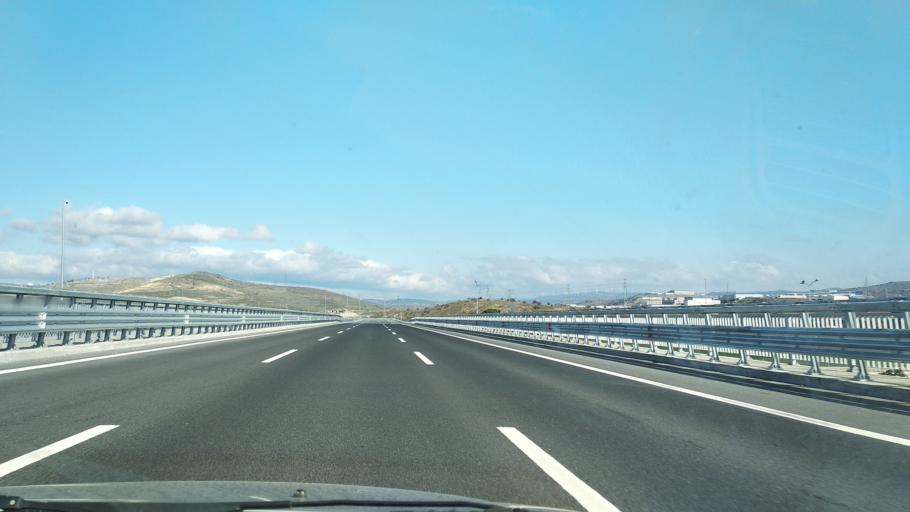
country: TR
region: Izmir
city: Aliaga
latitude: 38.8120
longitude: 27.0233
